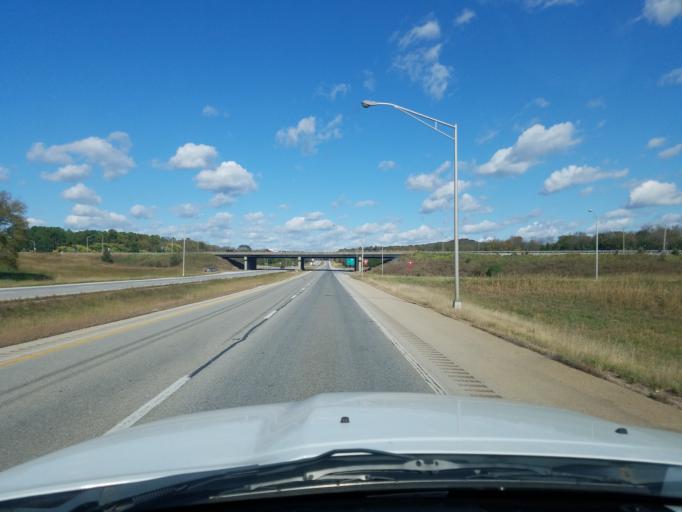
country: US
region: Kentucky
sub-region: Warren County
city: Bowling Green
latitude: 36.9905
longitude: -86.5035
